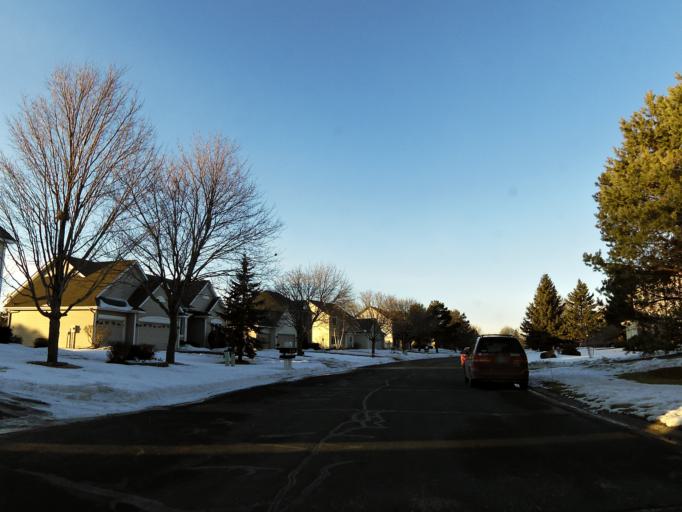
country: US
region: Minnesota
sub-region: Washington County
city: Woodbury
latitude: 44.8926
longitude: -92.8994
